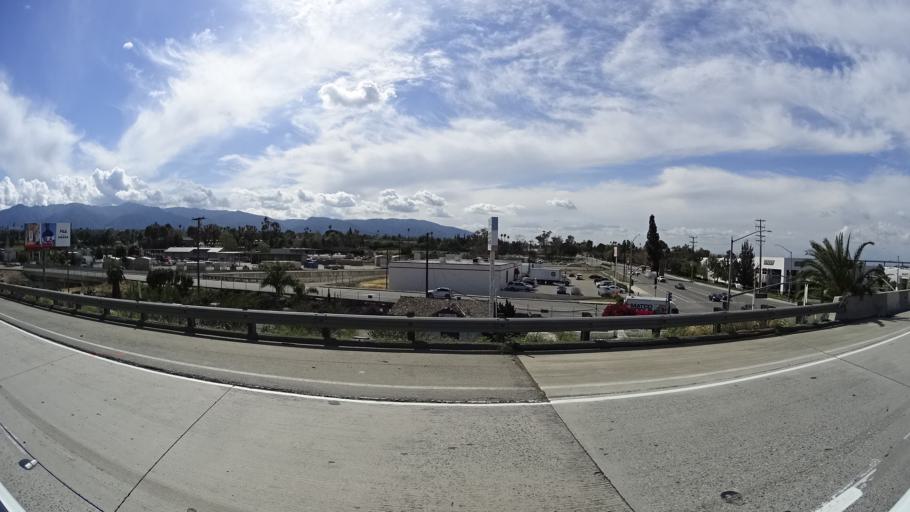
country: US
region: California
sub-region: Riverside County
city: Corona
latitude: 33.8742
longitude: -117.5455
